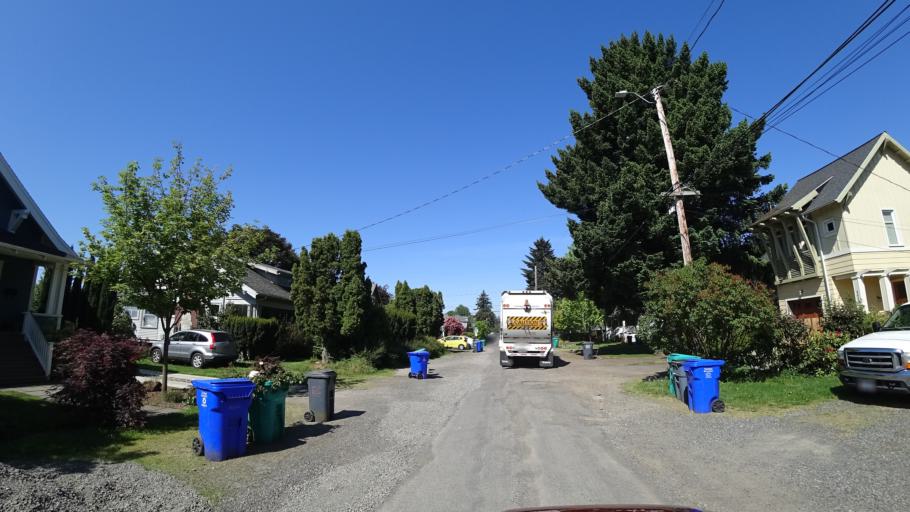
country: US
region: Oregon
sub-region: Multnomah County
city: Lents
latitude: 45.4913
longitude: -122.6029
